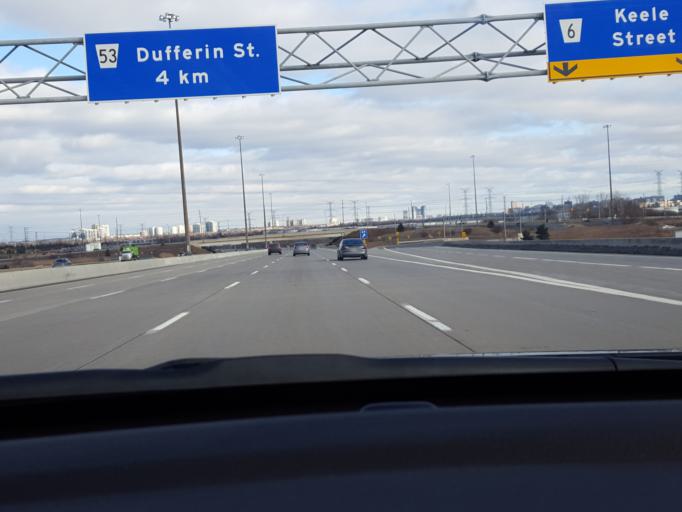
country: CA
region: Ontario
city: Concord
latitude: 43.7908
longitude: -79.5033
